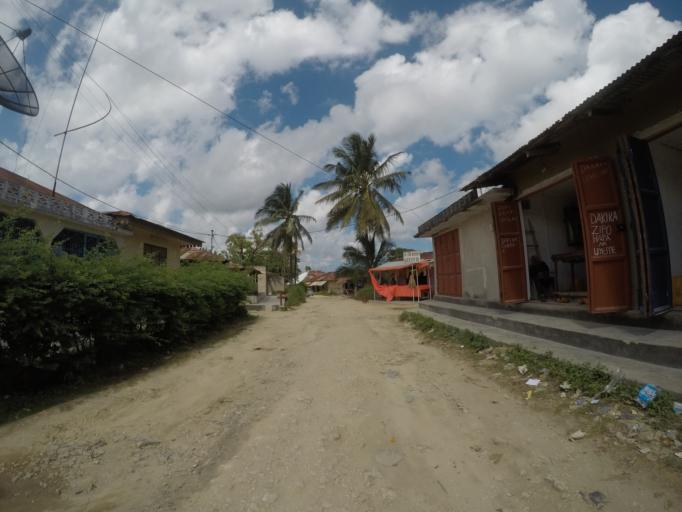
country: TZ
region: Pemba South
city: Chake Chake
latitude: -5.2359
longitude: 39.7794
